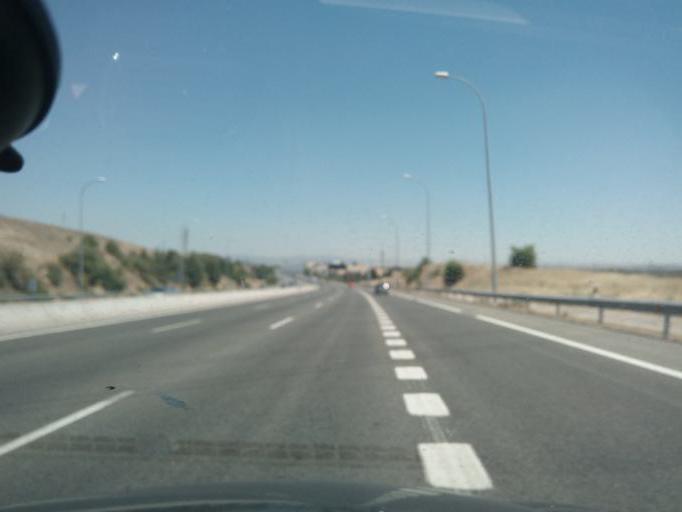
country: ES
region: Madrid
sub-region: Provincia de Madrid
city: San Sebastian de los Reyes
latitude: 40.5694
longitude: -3.5881
